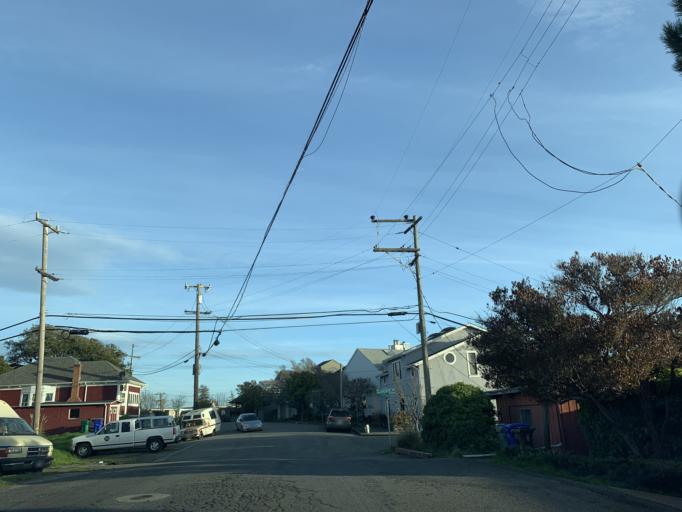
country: US
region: California
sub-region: Contra Costa County
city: North Richmond
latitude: 37.9288
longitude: -122.3922
